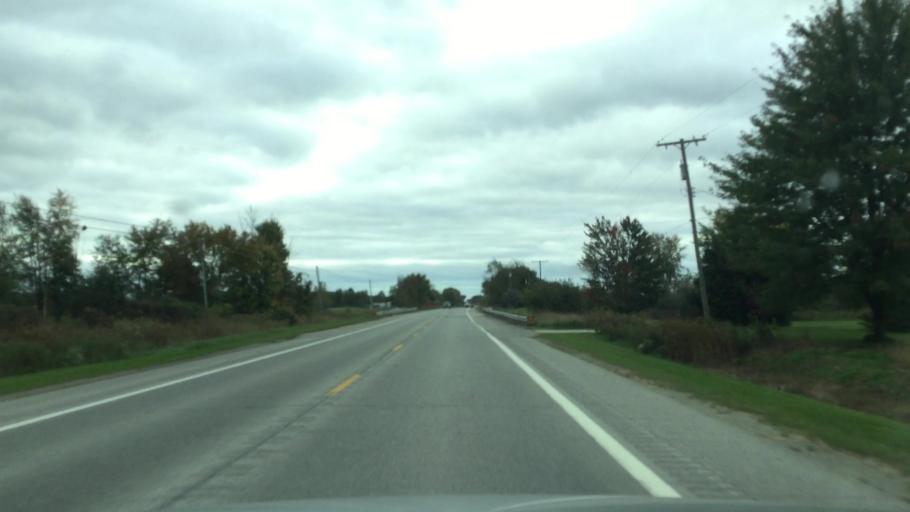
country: US
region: Michigan
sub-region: Macomb County
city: Memphis
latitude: 42.9677
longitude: -82.7639
